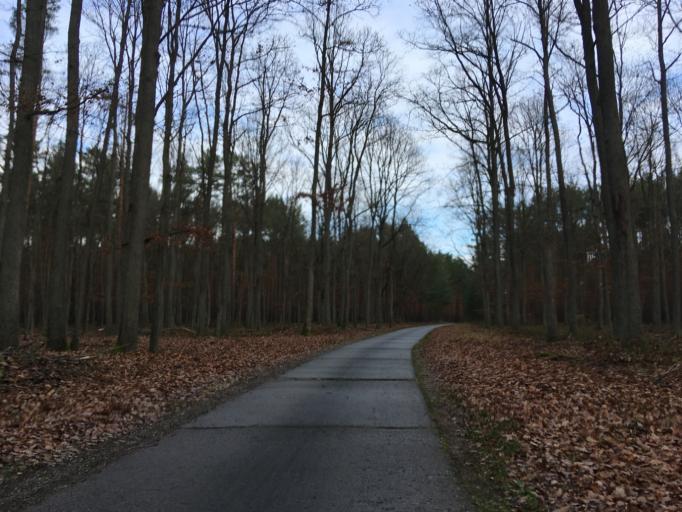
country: DE
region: Brandenburg
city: Tauer
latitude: 51.9554
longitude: 14.5216
